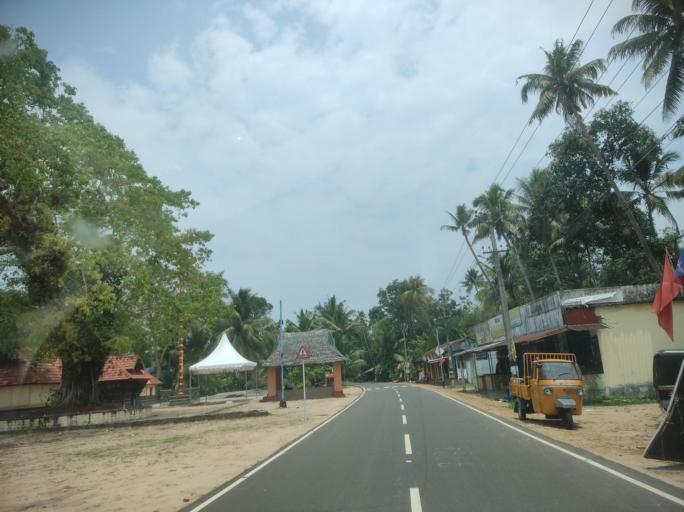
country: IN
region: Kerala
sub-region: Alappuzha
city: Vayalar
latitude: 9.7156
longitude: 76.3278
